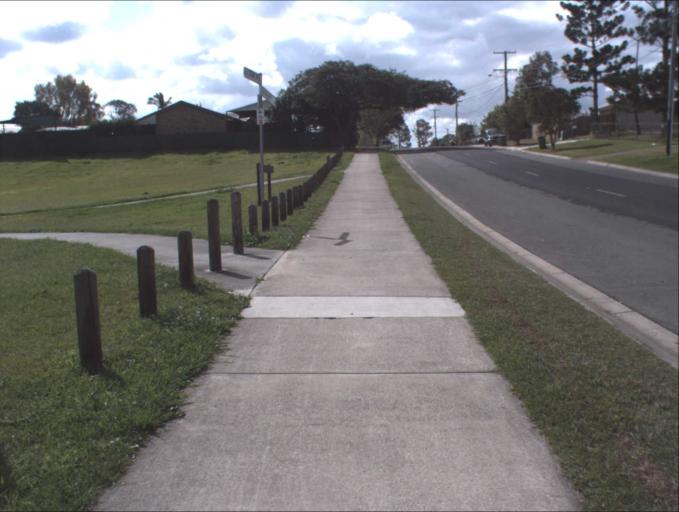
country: AU
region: Queensland
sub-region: Logan
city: Waterford West
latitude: -27.6936
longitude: 153.1285
